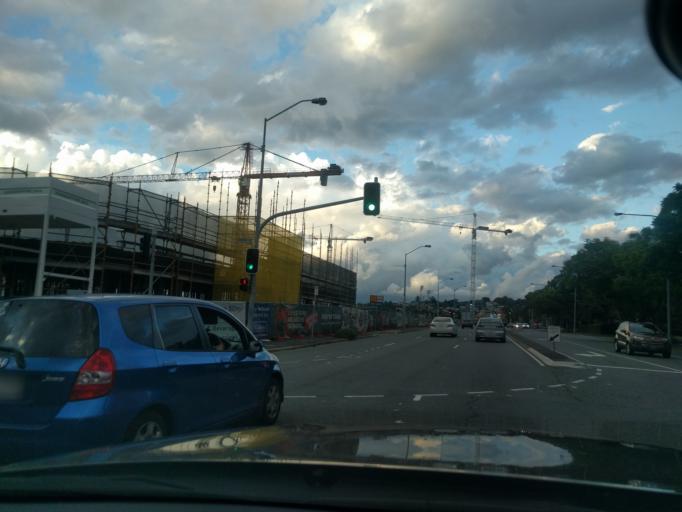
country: AU
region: Queensland
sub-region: Brisbane
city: Windsor
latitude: -27.4441
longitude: 153.0434
